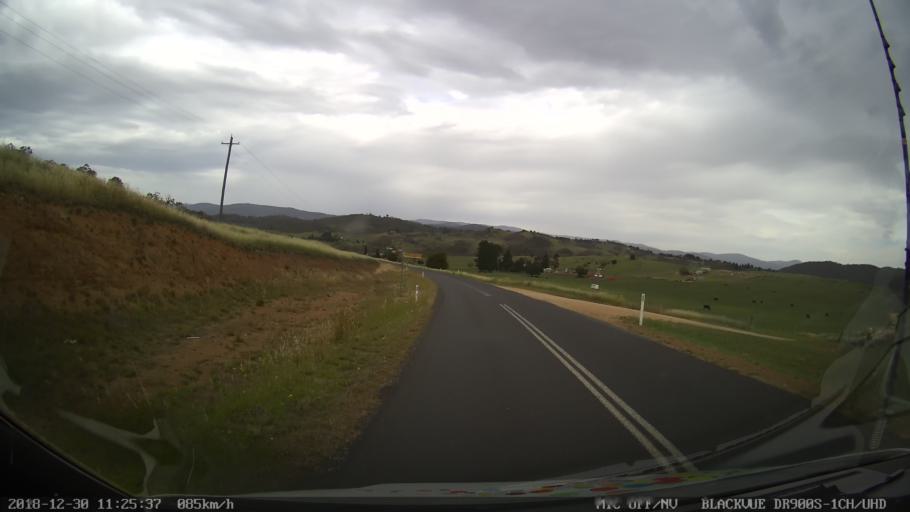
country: AU
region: New South Wales
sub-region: Snowy River
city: Jindabyne
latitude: -36.4693
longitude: 148.6460
